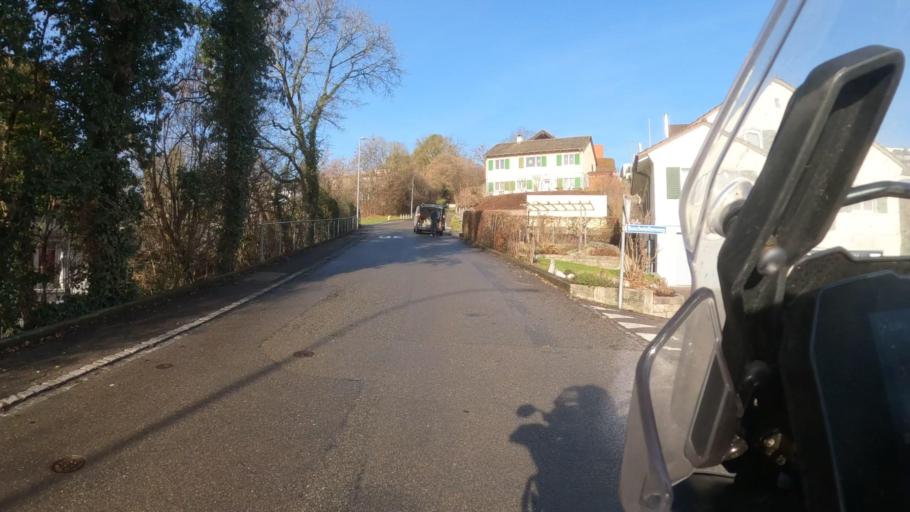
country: CH
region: Schaffhausen
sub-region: Bezirk Reiat
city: Thayngen
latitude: 47.7539
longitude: 8.7055
